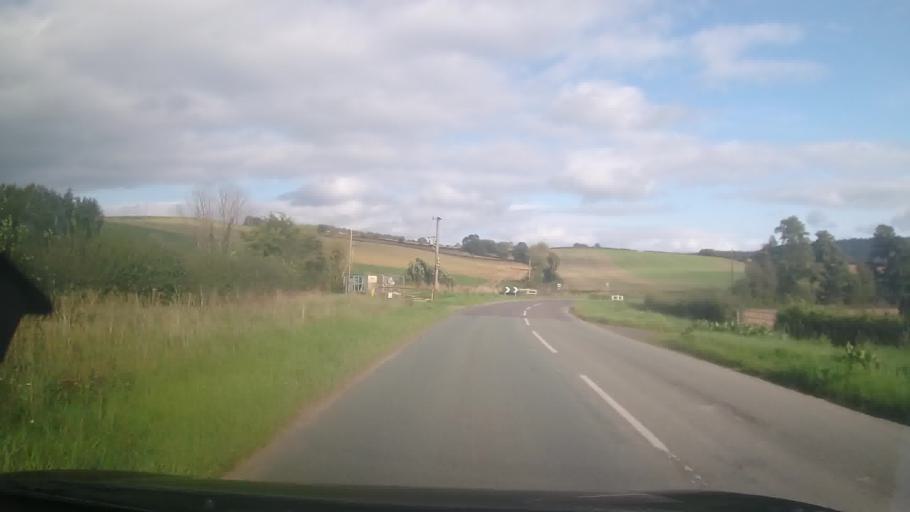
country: GB
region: England
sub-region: Shropshire
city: Lydham
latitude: 52.4676
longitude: -2.9370
